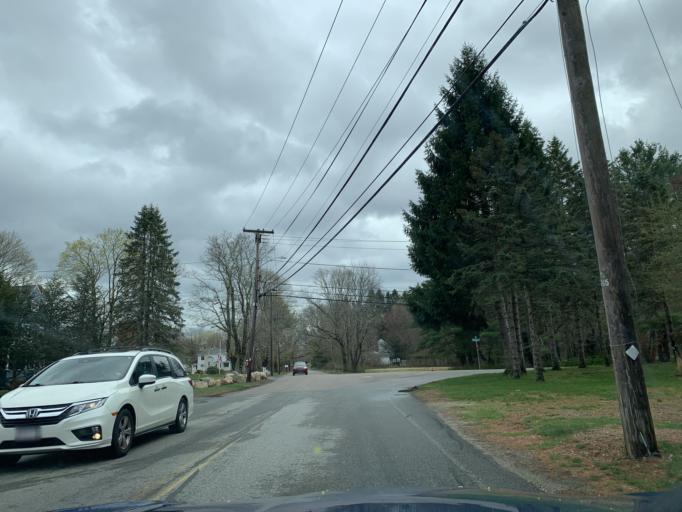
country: US
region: Massachusetts
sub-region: Bristol County
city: Norton
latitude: 41.9577
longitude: -71.2358
